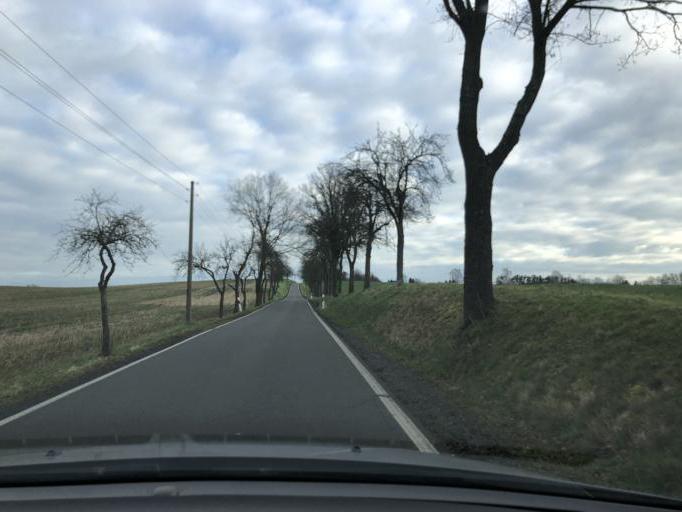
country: DE
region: Saxony
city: Zschadrass
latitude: 51.1975
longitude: 12.8139
